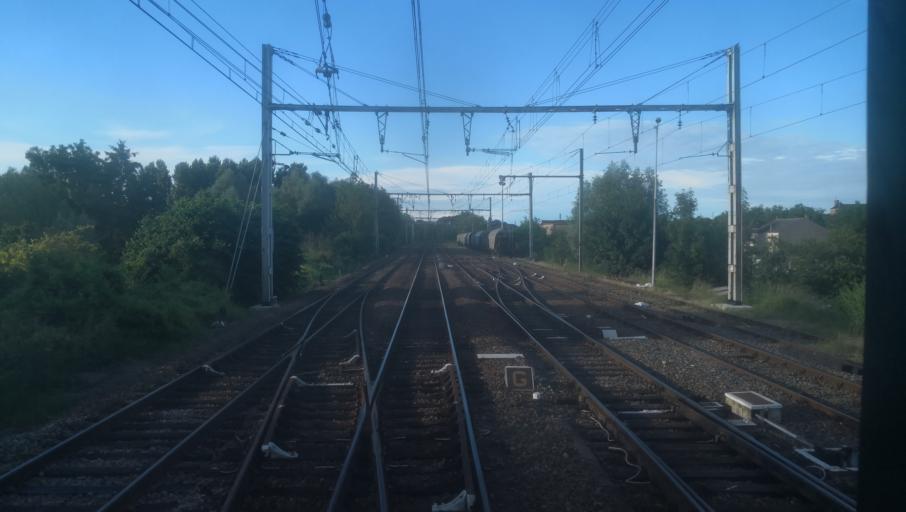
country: FR
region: Centre
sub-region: Departement de l'Indre
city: Issoudun
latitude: 46.9519
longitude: 1.9876
